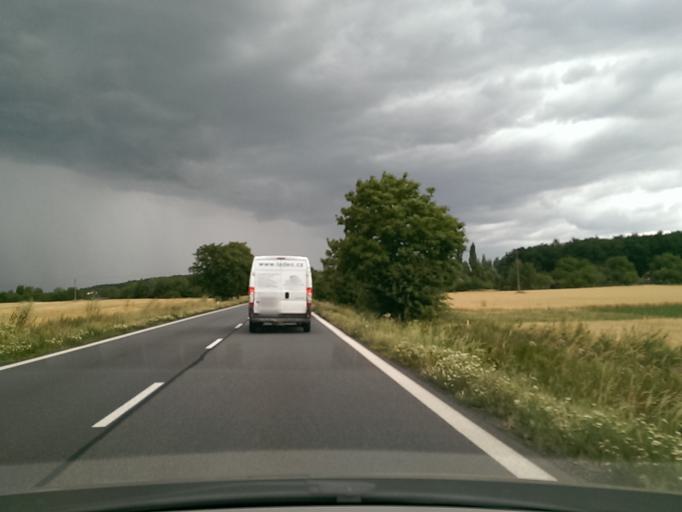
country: CZ
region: Central Bohemia
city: Loucen
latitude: 50.2539
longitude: 14.9902
